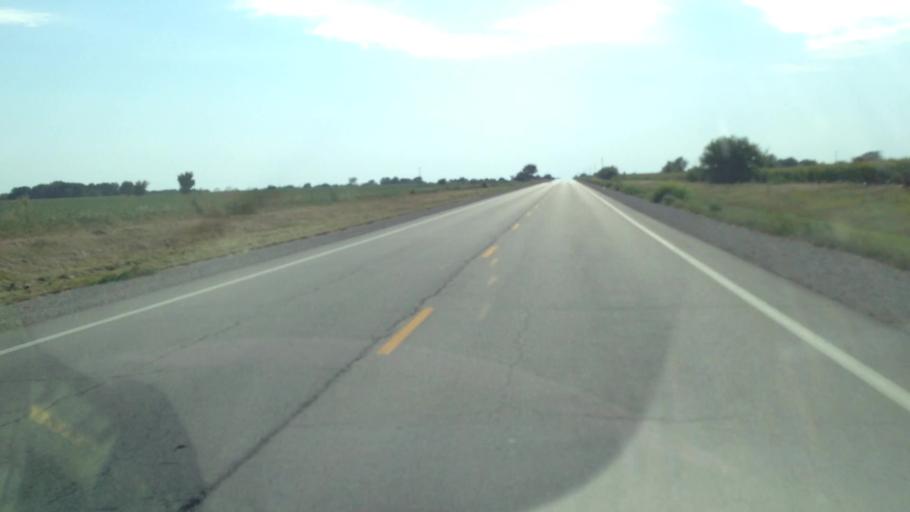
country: US
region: Kansas
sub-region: Anderson County
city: Garnett
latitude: 38.0816
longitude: -95.2011
